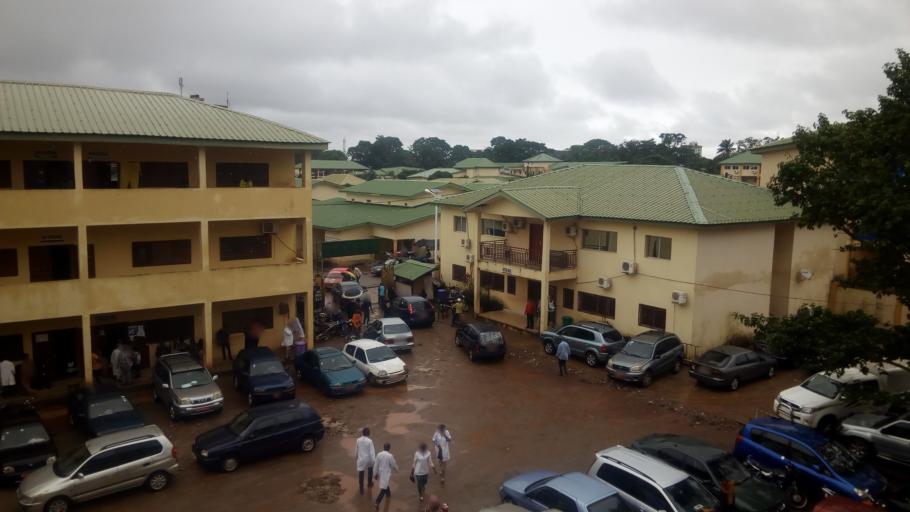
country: GN
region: Conakry
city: Camayenne
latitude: 9.5373
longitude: -13.6864
